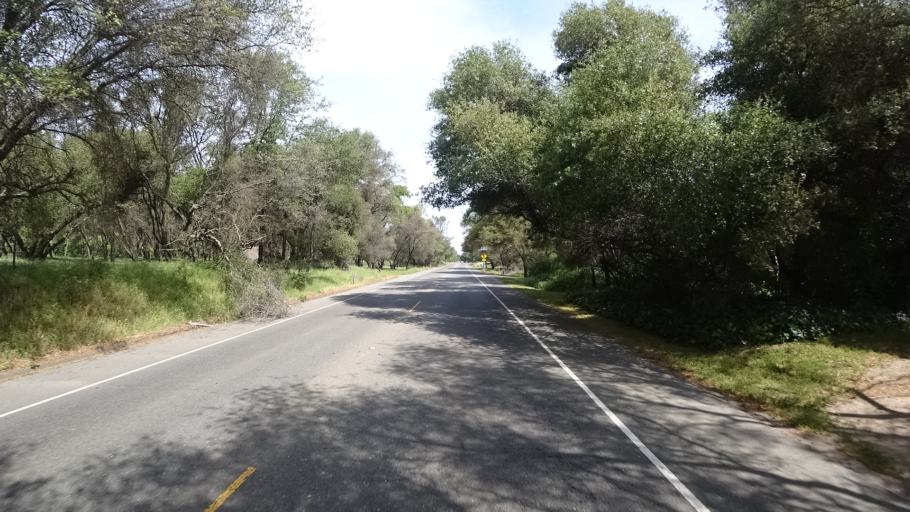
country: US
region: California
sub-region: Placer County
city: Loomis
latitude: 38.8222
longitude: -121.2173
